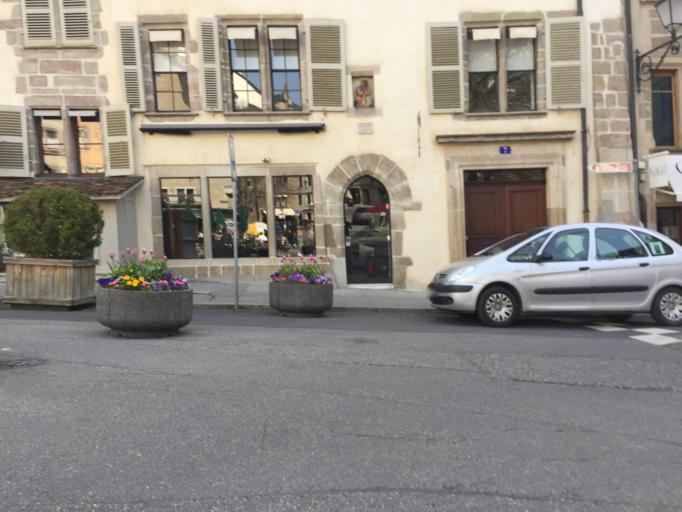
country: CH
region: Geneva
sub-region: Geneva
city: Geneve
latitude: 46.2001
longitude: 6.1490
